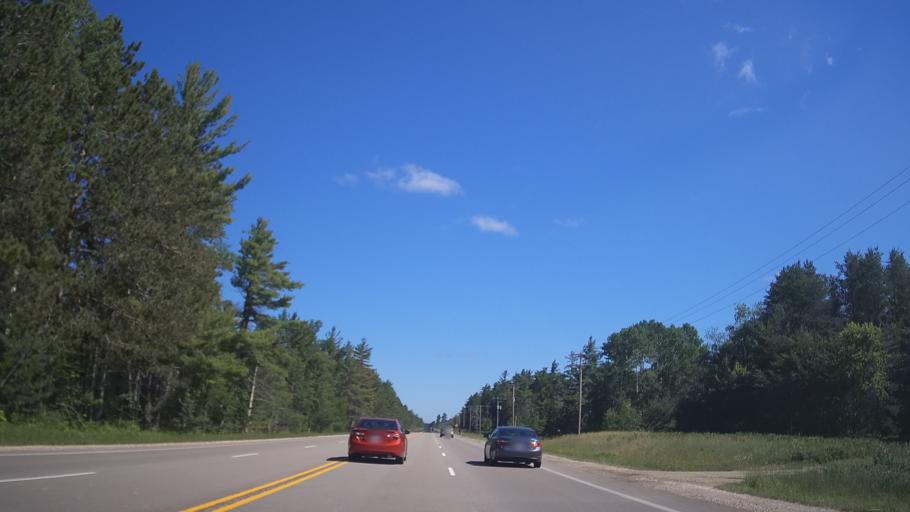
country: US
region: Michigan
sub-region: Cheboygan County
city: Indian River
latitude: 45.5156
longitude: -84.7815
